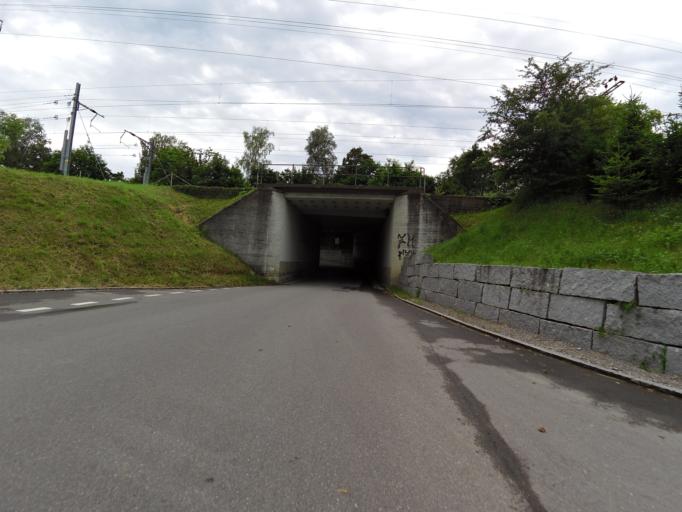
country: CH
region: Thurgau
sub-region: Frauenfeld District
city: Gachnang
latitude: 47.5518
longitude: 8.8608
